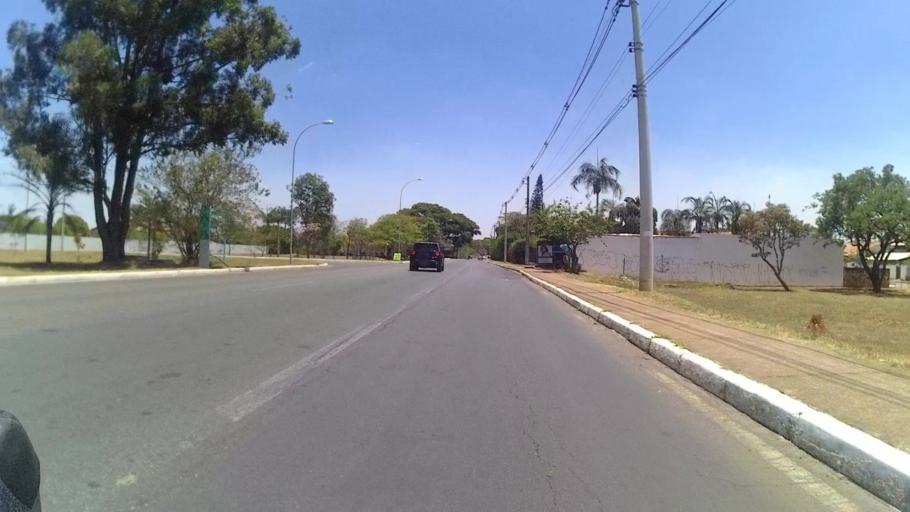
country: BR
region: Federal District
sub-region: Brasilia
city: Brasilia
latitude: -15.7489
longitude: -47.8449
